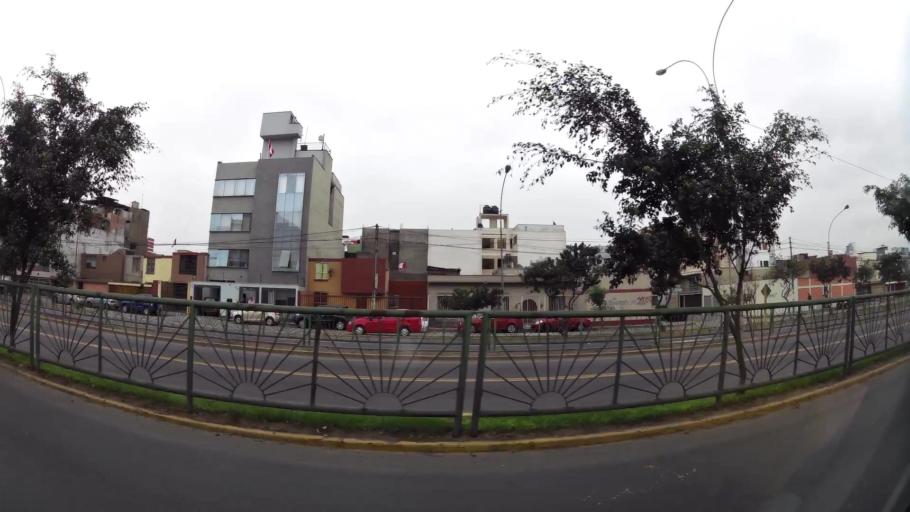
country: PE
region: Lima
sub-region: Lima
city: Surco
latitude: -12.1200
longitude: -77.0064
